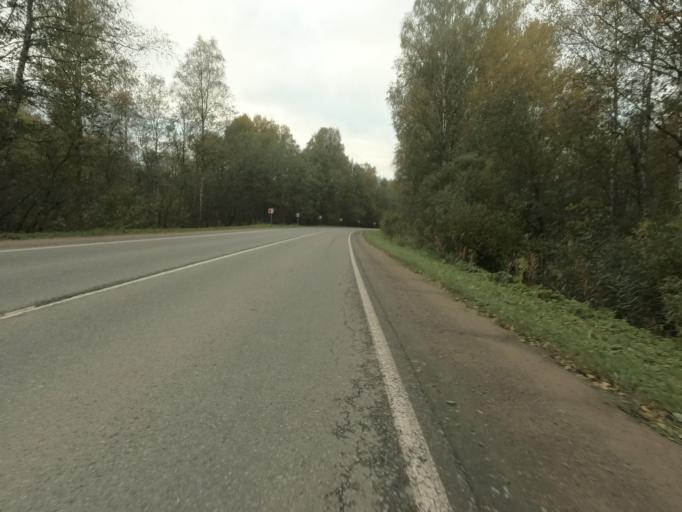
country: RU
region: Leningrad
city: Pavlovo
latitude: 59.7969
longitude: 30.9464
